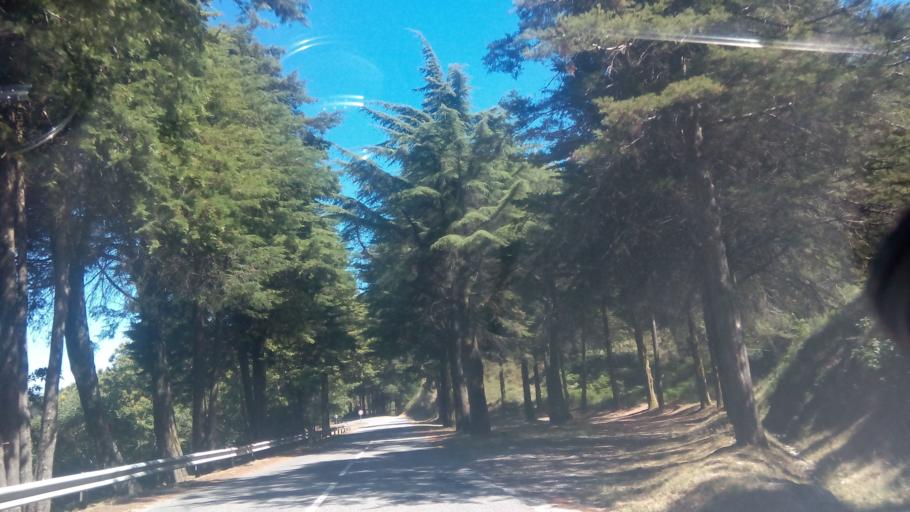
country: PT
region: Vila Real
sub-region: Santa Marta de Penaguiao
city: Santa Marta de Penaguiao
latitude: 41.2819
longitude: -7.8815
